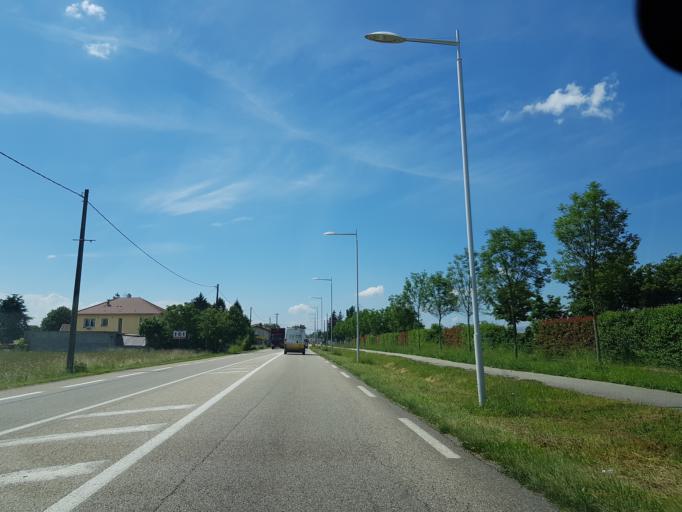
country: FR
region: Rhone-Alpes
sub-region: Departement de l'Ain
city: Montagnat
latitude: 46.1967
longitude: 5.2648
